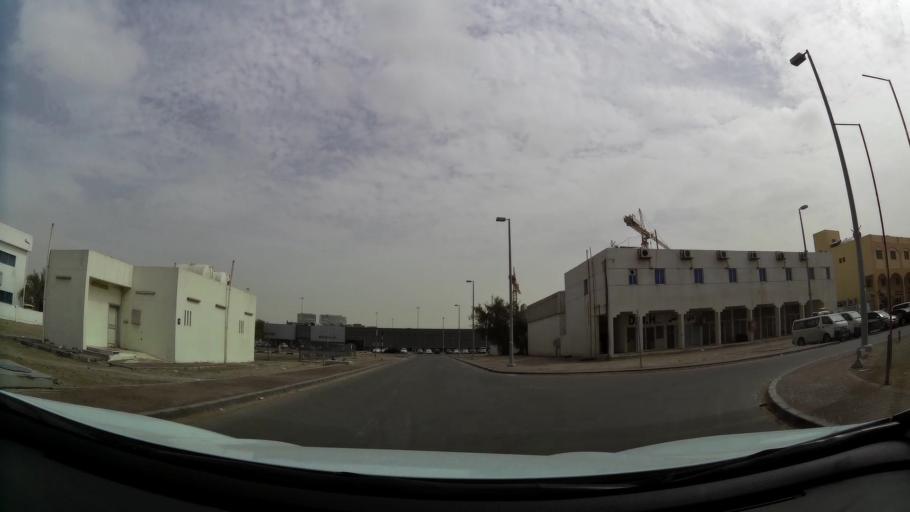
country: AE
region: Abu Dhabi
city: Abu Dhabi
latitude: 24.3720
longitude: 54.5204
